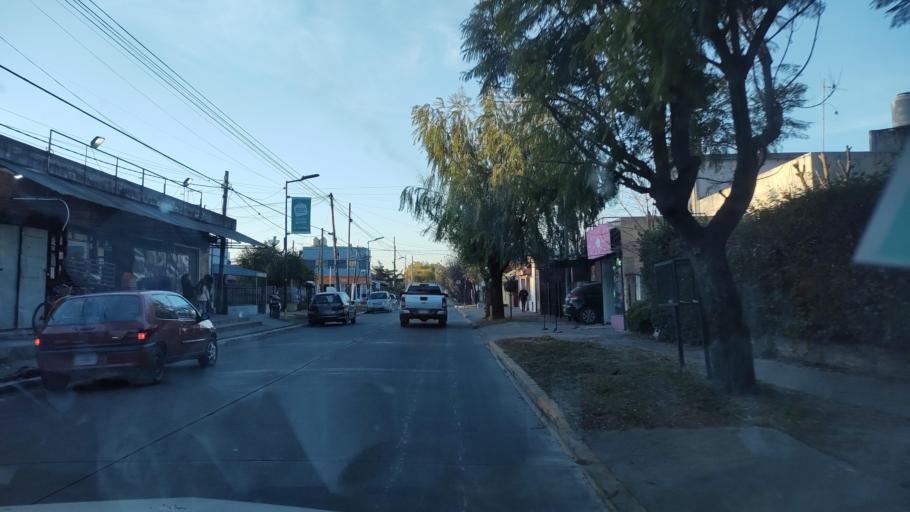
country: AR
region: Buenos Aires
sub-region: Partido de La Plata
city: La Plata
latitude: -34.9013
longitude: -58.0434
